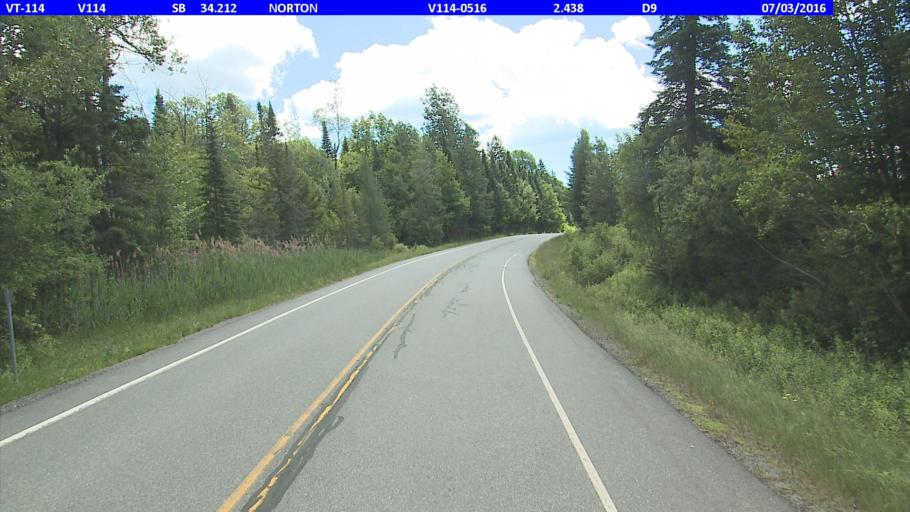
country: CA
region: Quebec
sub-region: Estrie
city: Coaticook
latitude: 44.9712
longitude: -71.8163
